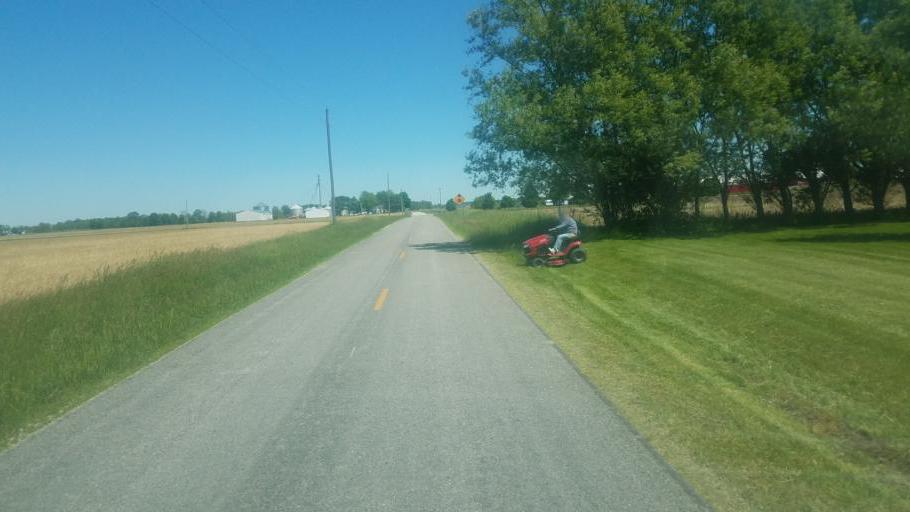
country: US
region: Ohio
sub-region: Shelby County
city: Sidney
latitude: 40.2085
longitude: -84.0803
